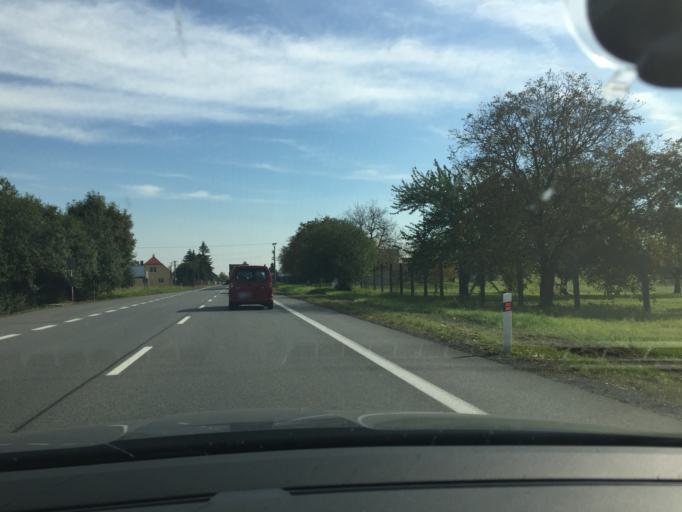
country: CZ
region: Central Bohemia
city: Cerhenice
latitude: 50.0453
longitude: 15.0723
